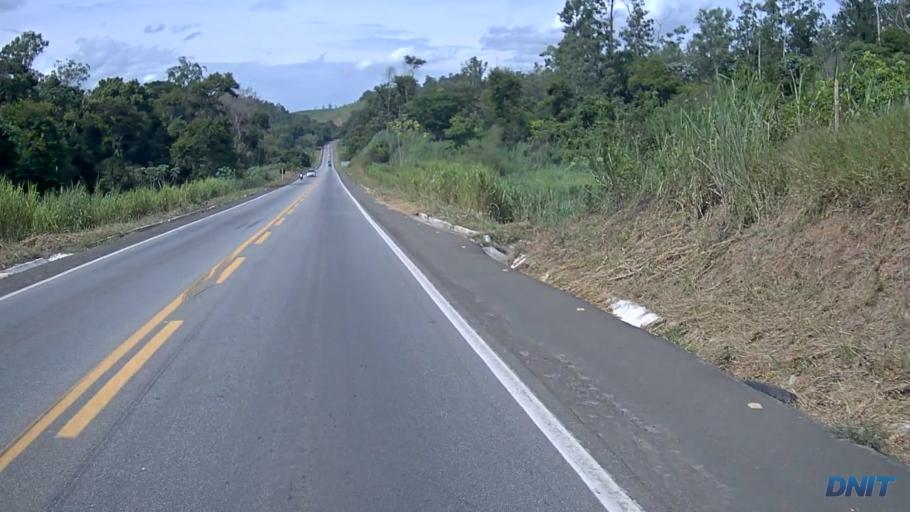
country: BR
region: Minas Gerais
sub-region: Ipatinga
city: Ipatinga
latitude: -19.4325
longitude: -42.5065
